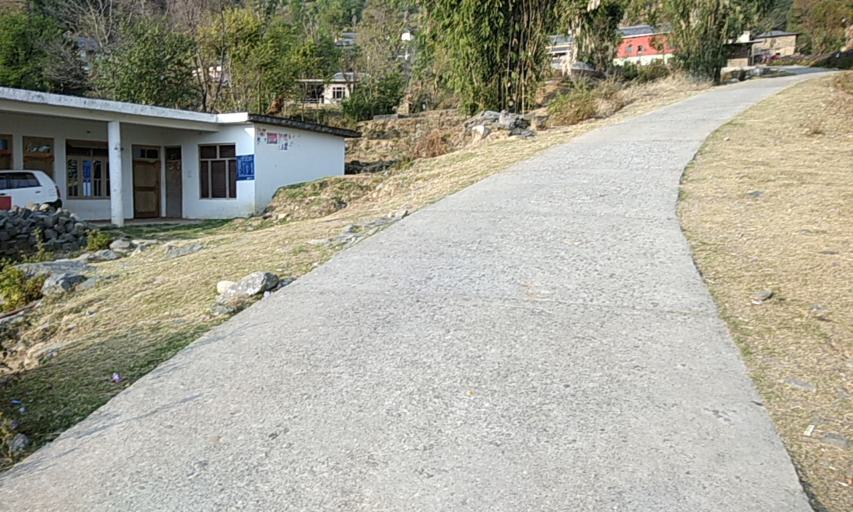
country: IN
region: Himachal Pradesh
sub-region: Kangra
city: Palampur
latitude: 32.1198
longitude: 76.5853
